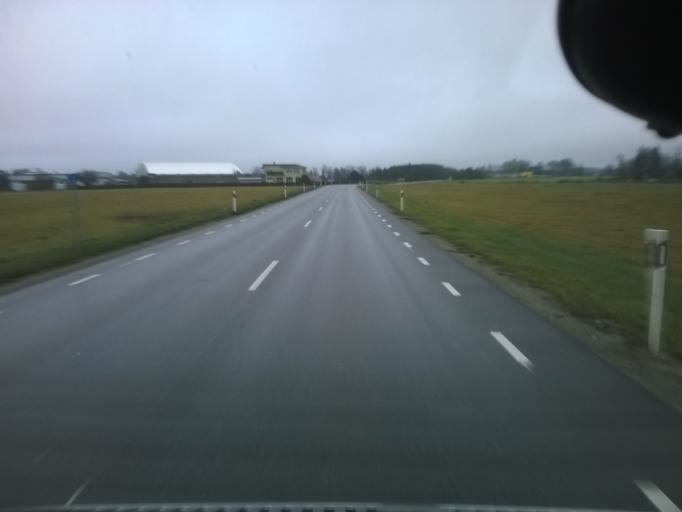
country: EE
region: Harju
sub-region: Saku vald
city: Saku
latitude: 59.2661
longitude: 24.7242
